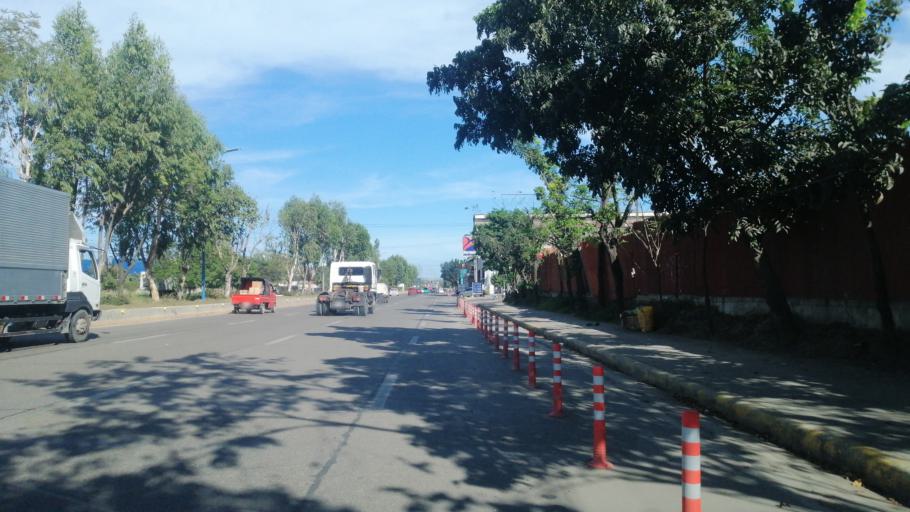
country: PH
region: Central Visayas
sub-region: Lapu-Lapu City
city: Buagsong
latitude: 10.3257
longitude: 123.9381
